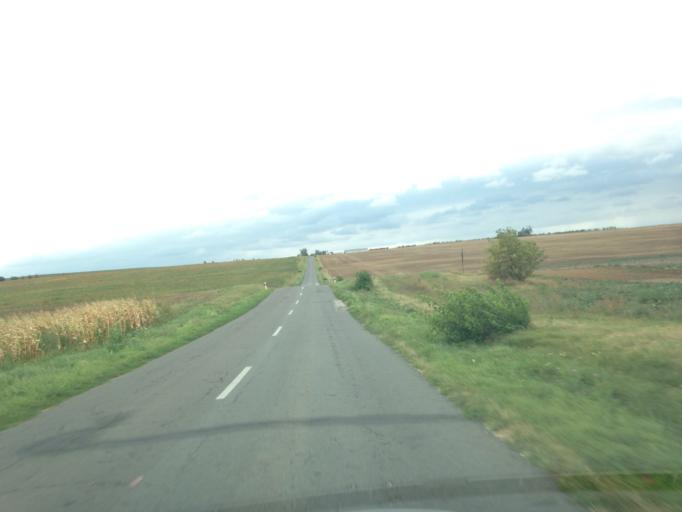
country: SK
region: Nitriansky
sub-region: Okres Komarno
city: Hurbanovo
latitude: 47.9059
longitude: 18.2832
